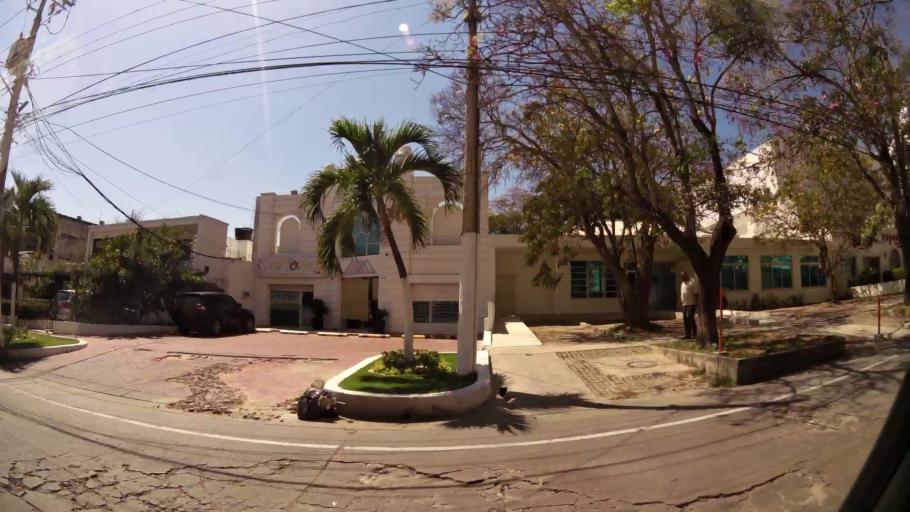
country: CO
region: Atlantico
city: Barranquilla
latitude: 11.0005
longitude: -74.8092
